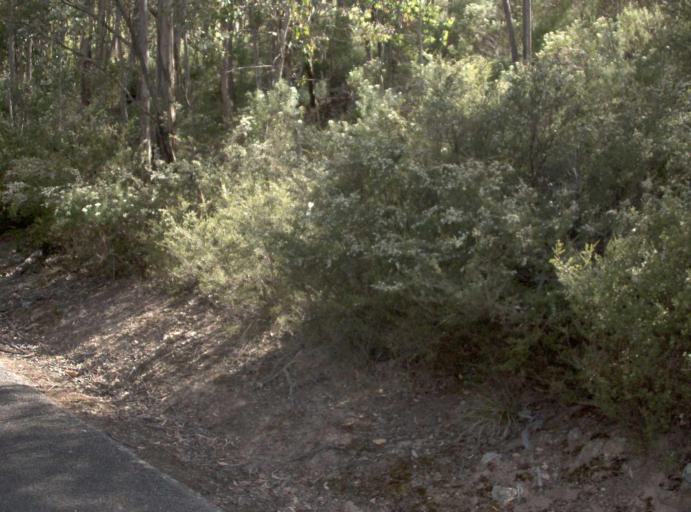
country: AU
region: Victoria
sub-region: East Gippsland
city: Lakes Entrance
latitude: -37.4820
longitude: 148.1262
